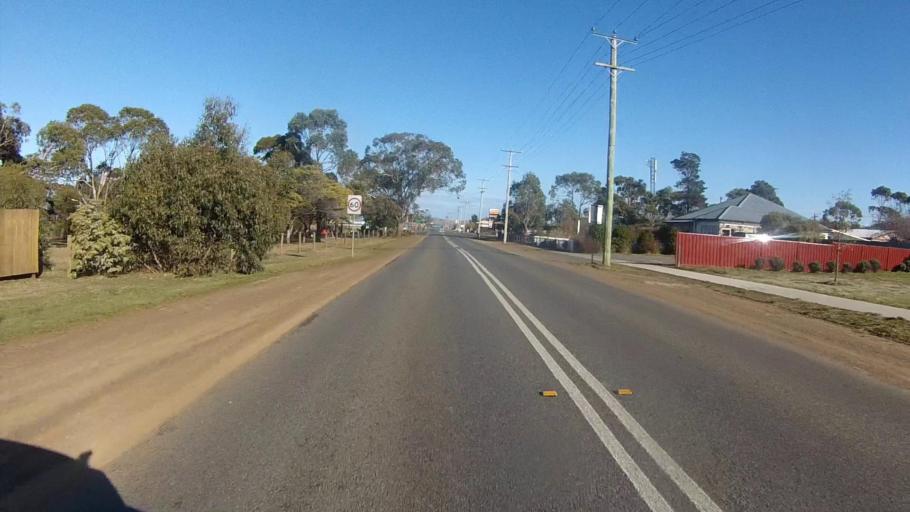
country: AU
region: Tasmania
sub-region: Sorell
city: Sorell
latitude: -42.8879
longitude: 147.8100
